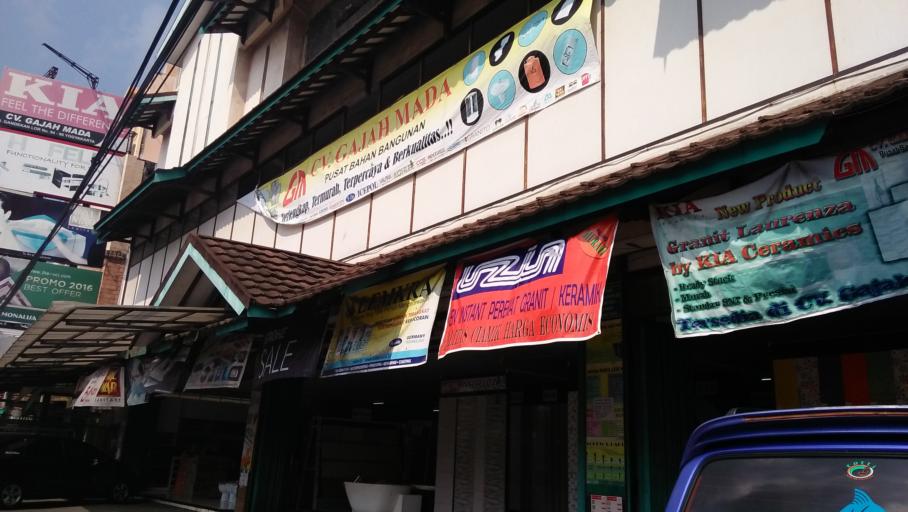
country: ID
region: Daerah Istimewa Yogyakarta
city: Yogyakarta
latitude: -7.7904
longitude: 110.3620
